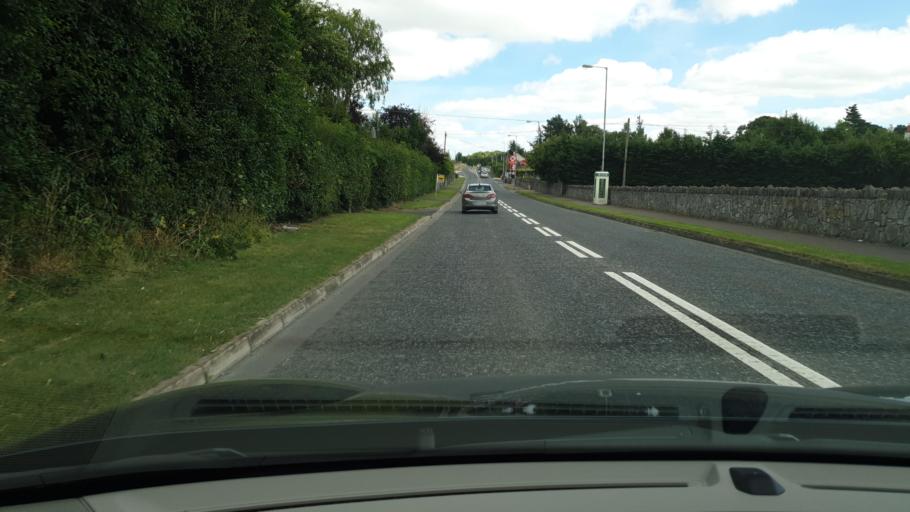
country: IE
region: Leinster
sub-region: An Mhi
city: Newtown Trim
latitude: 53.5266
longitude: -6.6744
